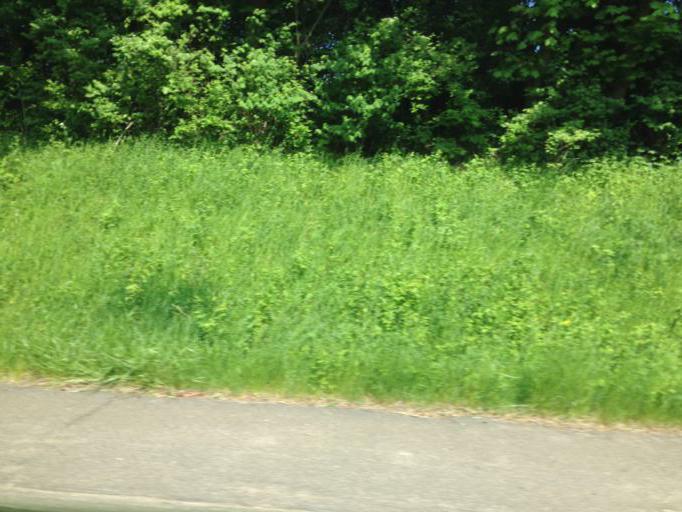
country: DE
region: North Rhine-Westphalia
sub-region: Regierungsbezirk Koln
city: Mechernich
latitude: 50.5648
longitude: 6.7020
